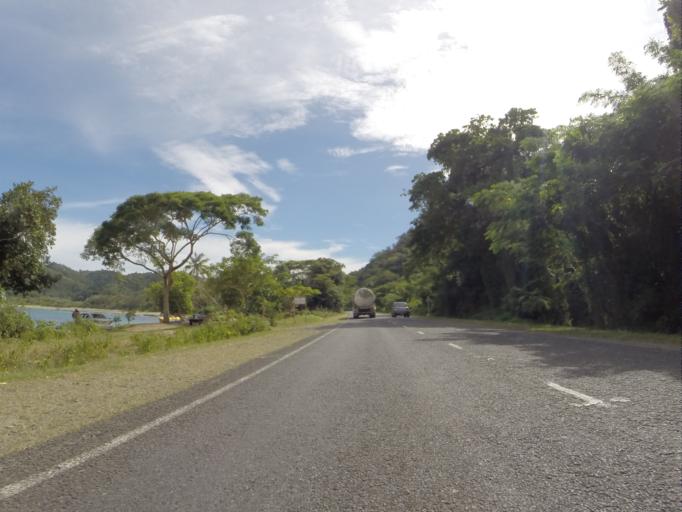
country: FJ
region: Western
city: Nadi
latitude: -18.1794
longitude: 177.5970
